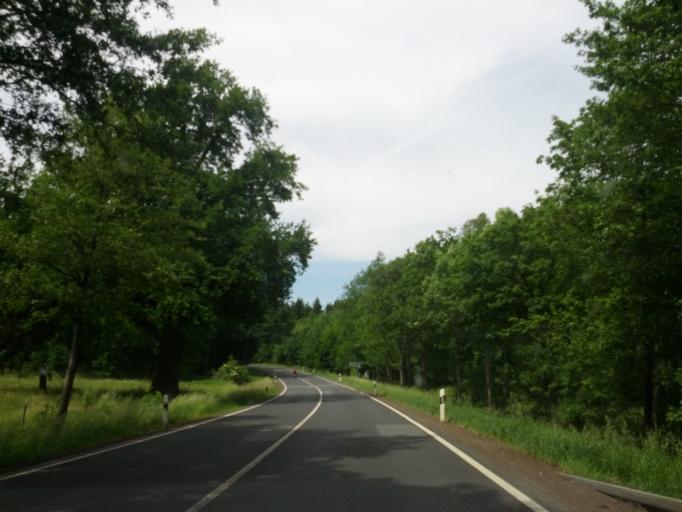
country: DE
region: Thuringia
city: Friedrichroda
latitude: 50.8671
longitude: 10.5423
